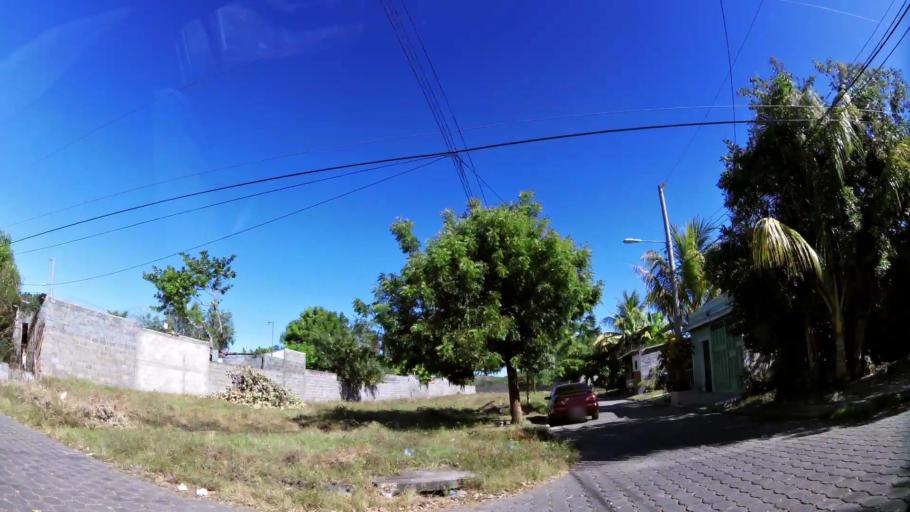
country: SV
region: San Miguel
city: San Miguel
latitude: 13.4693
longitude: -88.1513
